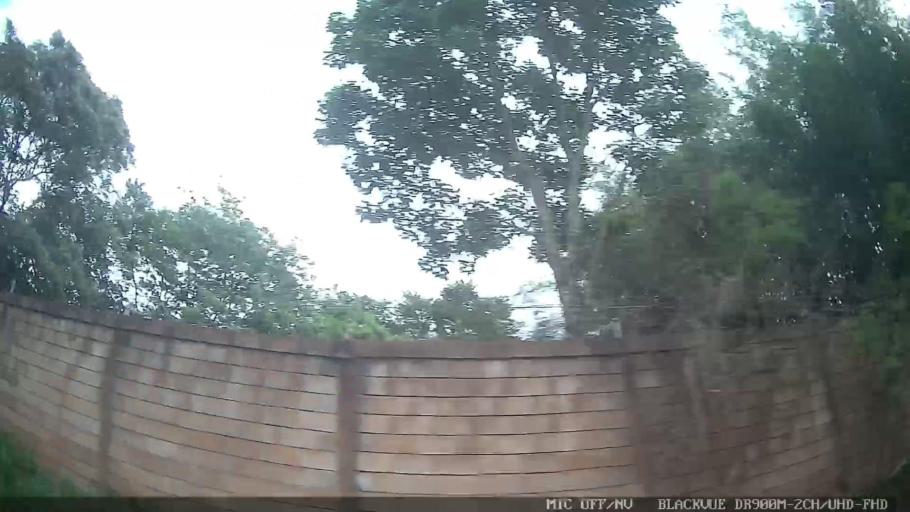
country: BR
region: Sao Paulo
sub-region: Jaguariuna
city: Jaguariuna
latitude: -22.7529
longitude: -47.0008
